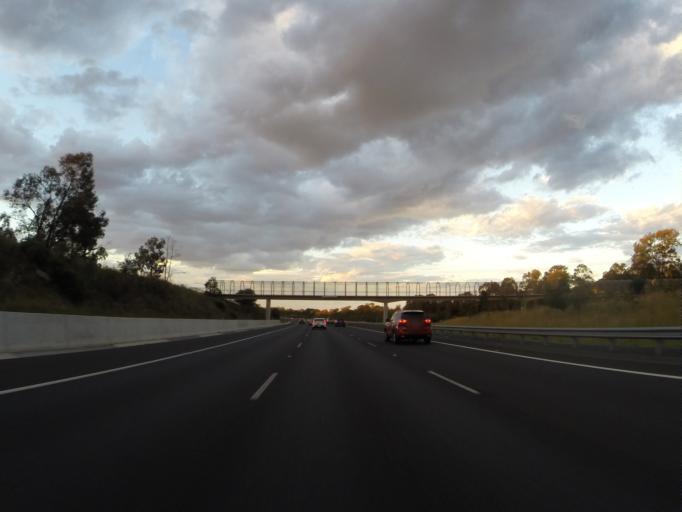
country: AU
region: New South Wales
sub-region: Campbelltown Municipality
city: Leumeah
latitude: -34.0463
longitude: 150.8182
